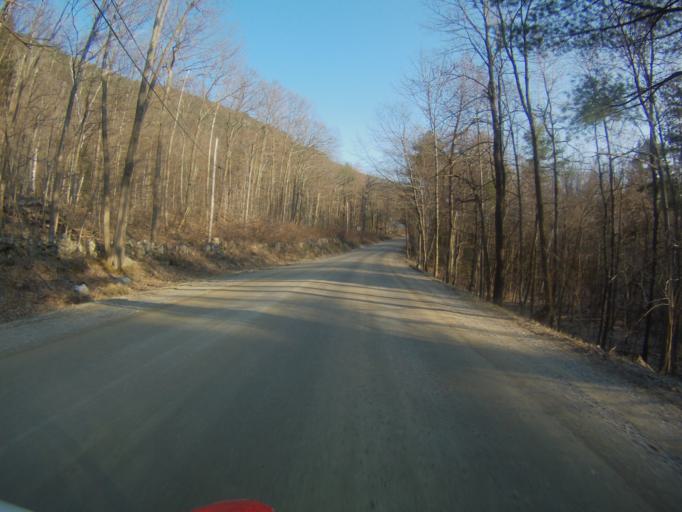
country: US
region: Vermont
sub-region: Addison County
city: Bristol
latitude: 44.1137
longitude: -73.0769
